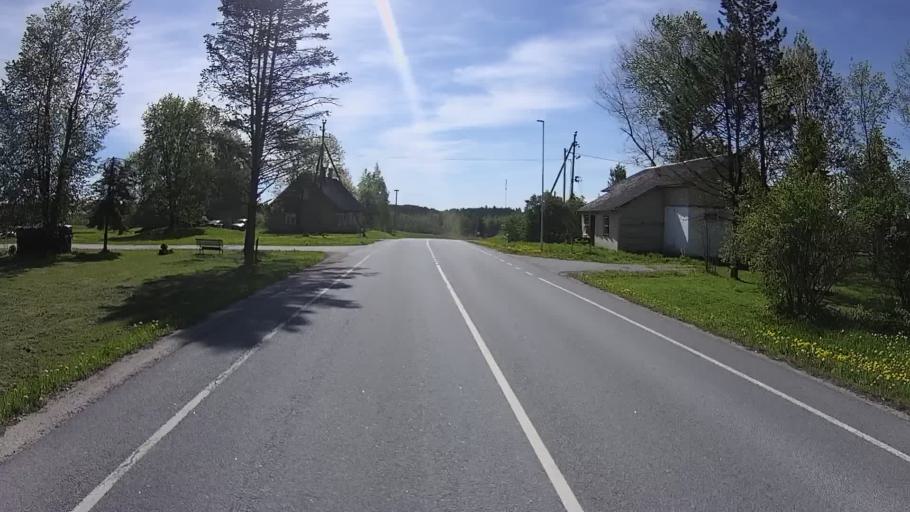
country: RU
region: Pskov
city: Pechory
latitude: 57.8484
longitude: 27.5822
